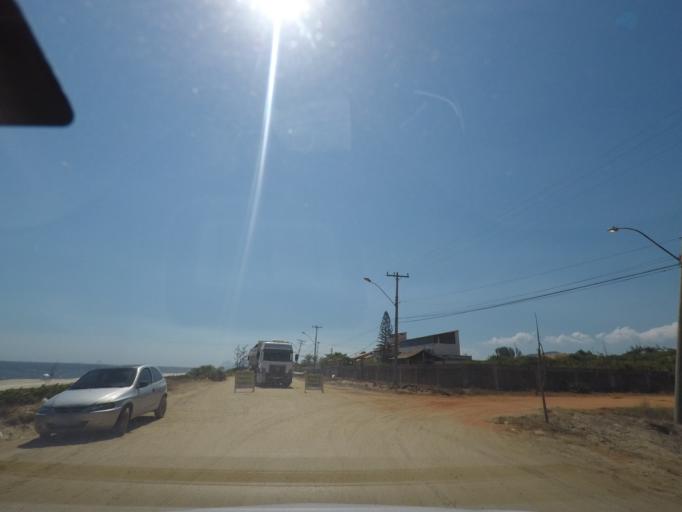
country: BR
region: Rio de Janeiro
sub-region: Marica
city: Marica
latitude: -22.9743
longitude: -42.9206
